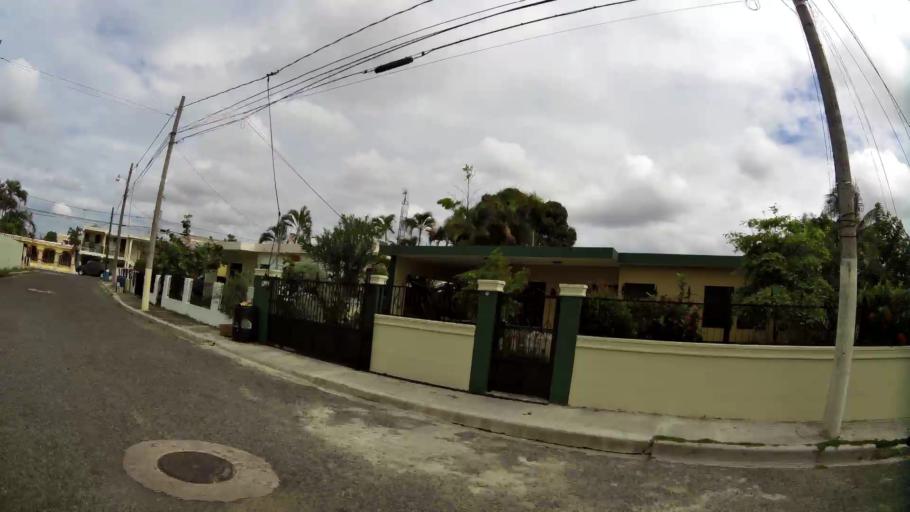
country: DO
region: Santiago
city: Santiago de los Caballeros
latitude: 19.4409
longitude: -70.6727
